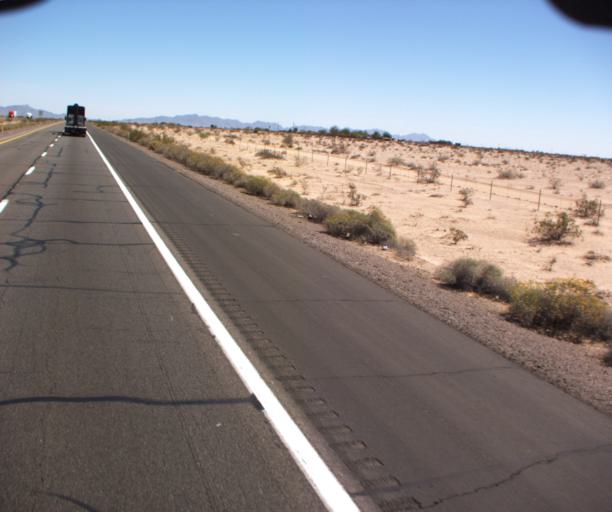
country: US
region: Arizona
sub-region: Yuma County
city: Wellton
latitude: 32.6851
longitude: -114.0041
